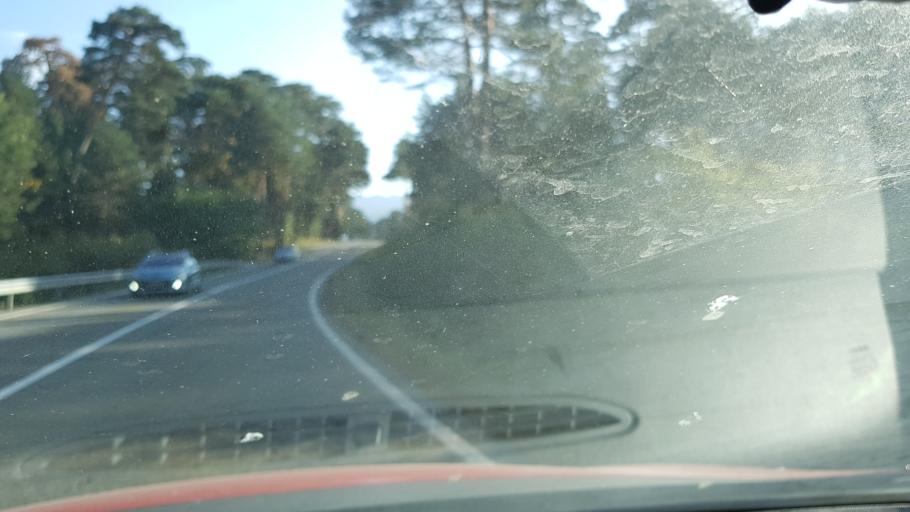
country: ES
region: Castille and Leon
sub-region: Provincia de Segovia
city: San Ildefonso
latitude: 40.8468
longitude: -4.0251
